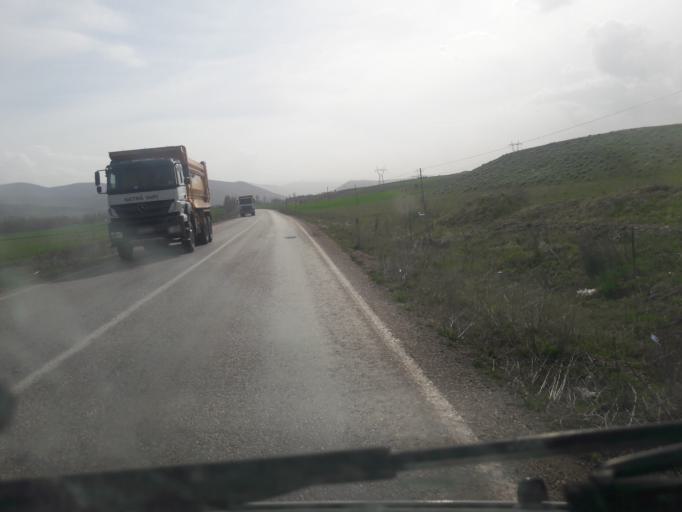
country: TR
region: Gumushane
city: Kelkit
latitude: 40.1383
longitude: 39.3859
